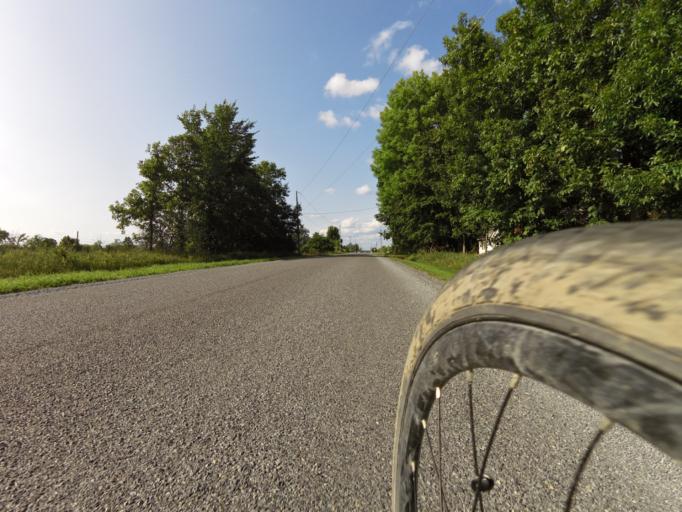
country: CA
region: Ontario
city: Kingston
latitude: 44.3984
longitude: -76.5962
